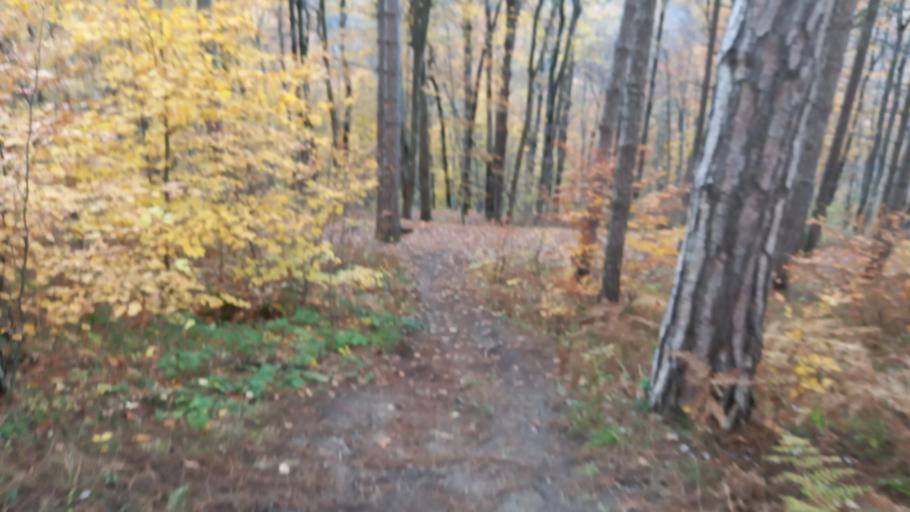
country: RU
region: Krasnodarskiy
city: Goryachiy Klyuch
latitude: 44.6127
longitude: 39.1032
